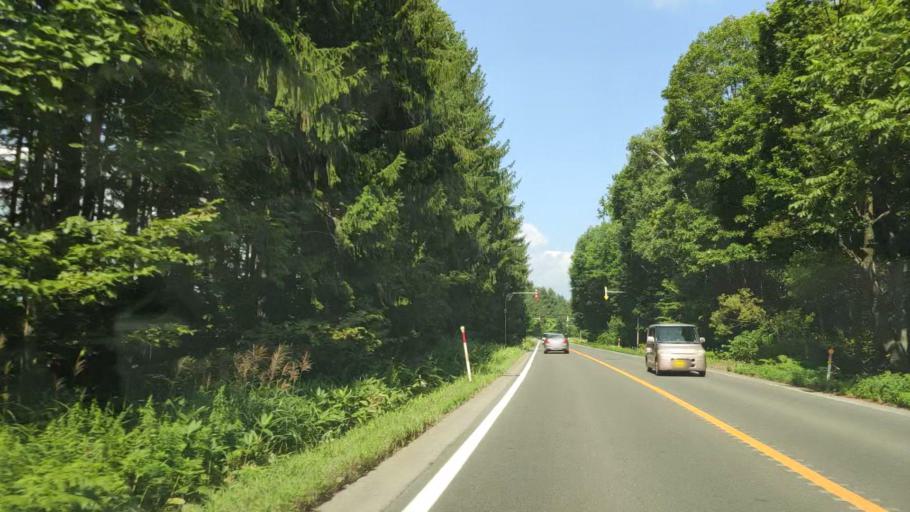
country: JP
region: Hokkaido
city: Shimo-furano
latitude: 43.5106
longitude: 142.4524
